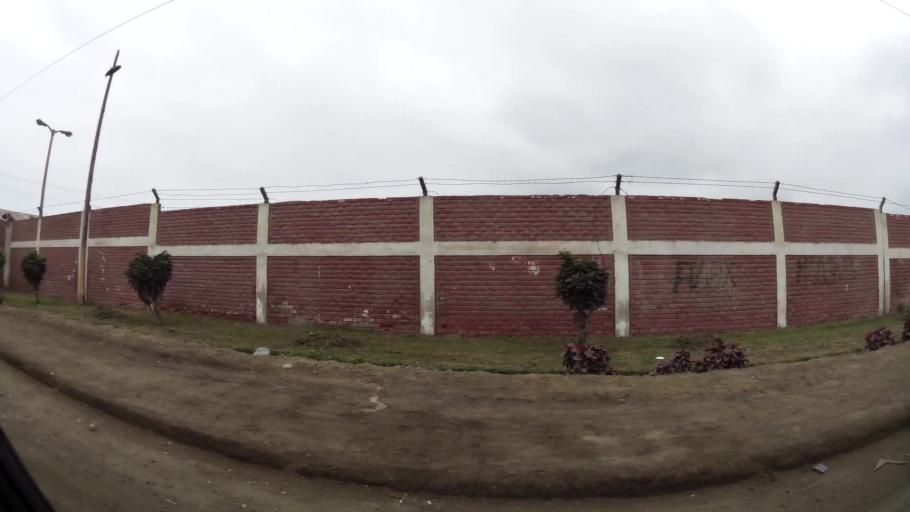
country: PE
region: Lima
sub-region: Barranca
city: Paramonga
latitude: -10.6778
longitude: -77.8222
